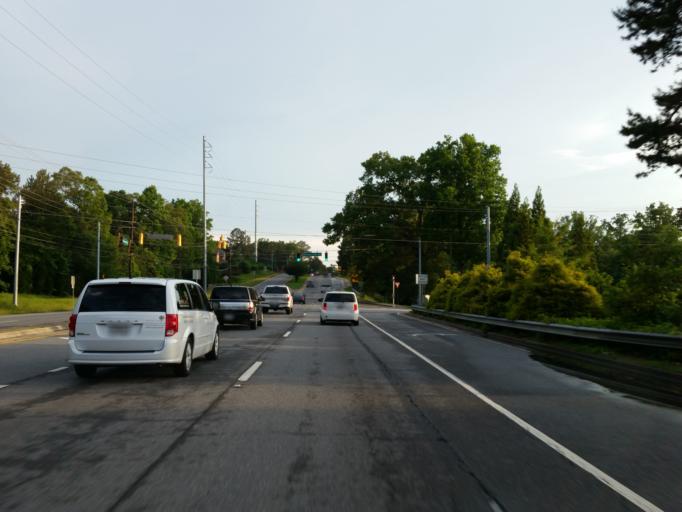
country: US
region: Georgia
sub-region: Fulton County
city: Roswell
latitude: 33.9988
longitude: -84.4071
